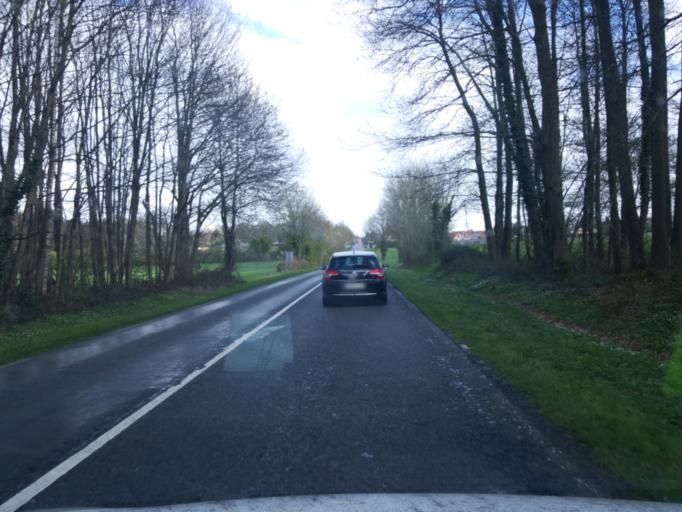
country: FR
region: Picardie
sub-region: Departement de l'Oise
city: Auneuil
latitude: 49.3501
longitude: 1.9349
